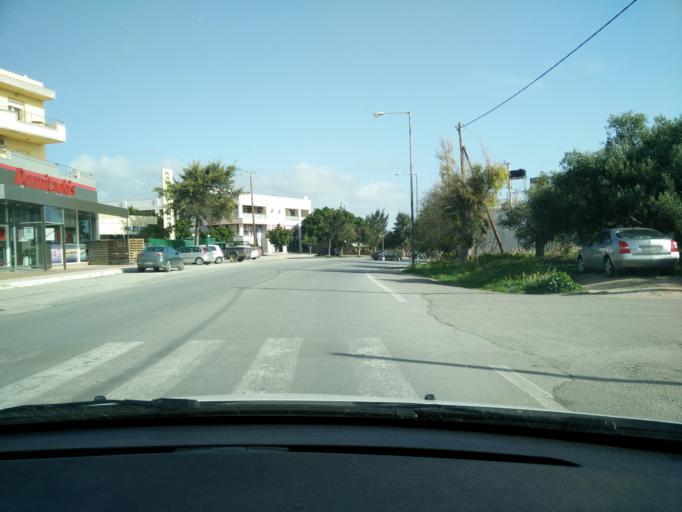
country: GR
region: Crete
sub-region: Nomos Lasithiou
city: Ierapetra
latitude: 35.0155
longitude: 25.7430
